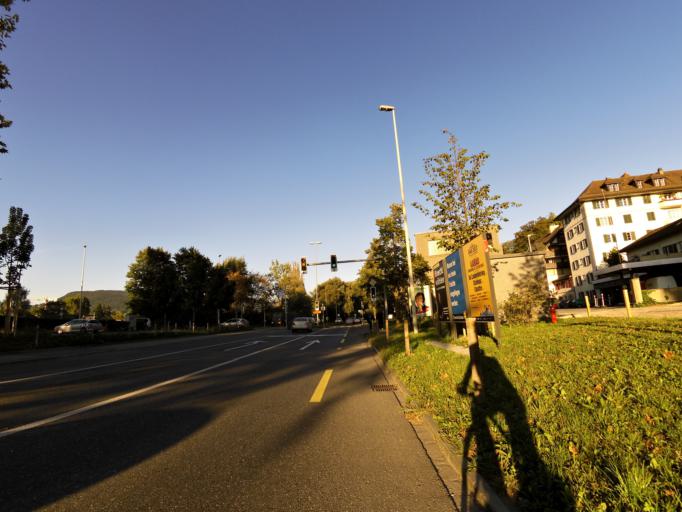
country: CH
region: Aargau
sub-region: Bezirk Aarau
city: Aarau
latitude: 47.3946
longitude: 8.0433
